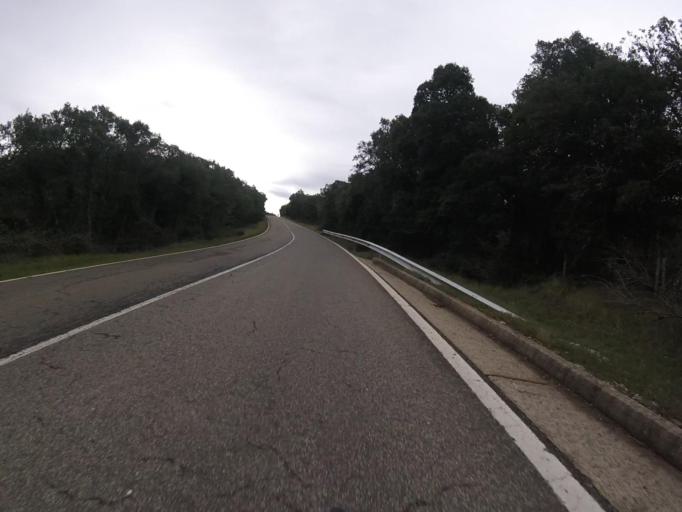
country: ES
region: Navarre
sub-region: Provincia de Navarra
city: Lezaun
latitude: 42.7590
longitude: -2.0128
